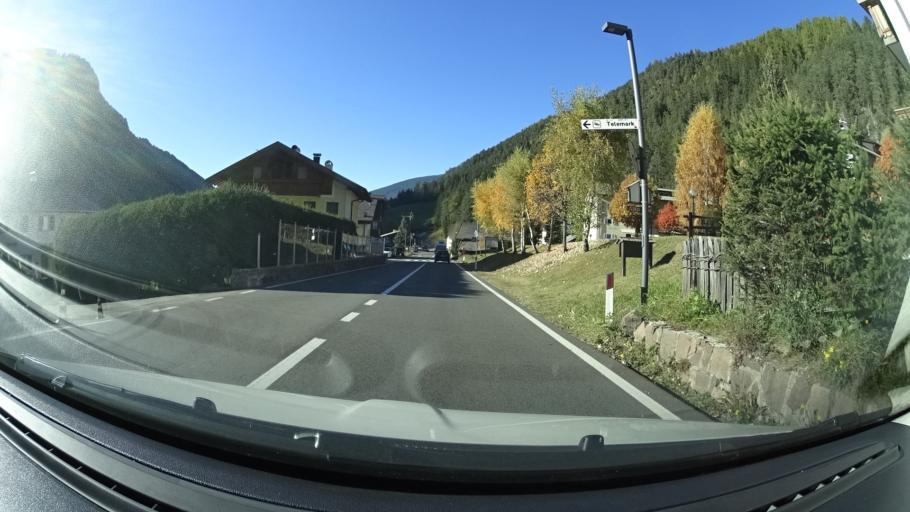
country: IT
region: Trentino-Alto Adige
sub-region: Bolzano
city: Santa Cristina Valgardena
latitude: 46.5594
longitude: 11.7094
